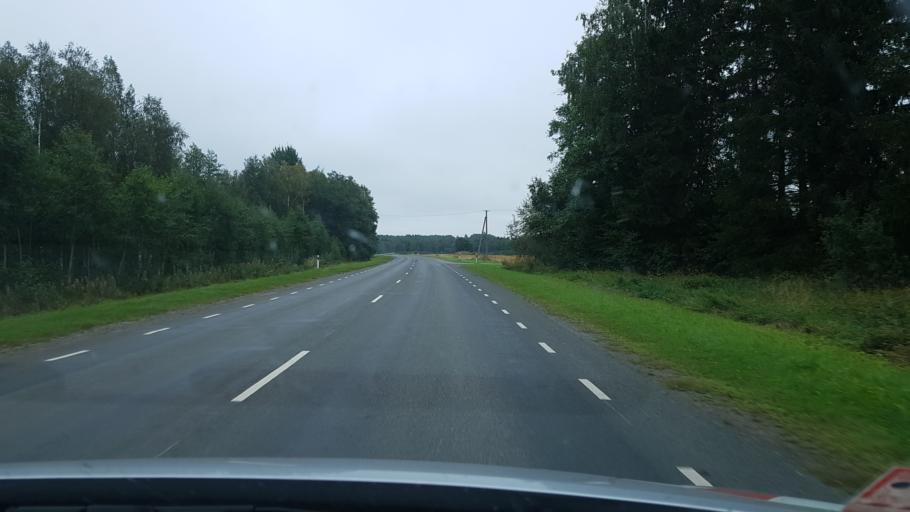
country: EE
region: Viljandimaa
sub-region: Suure-Jaani vald
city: Suure-Jaani
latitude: 58.5163
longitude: 25.5478
